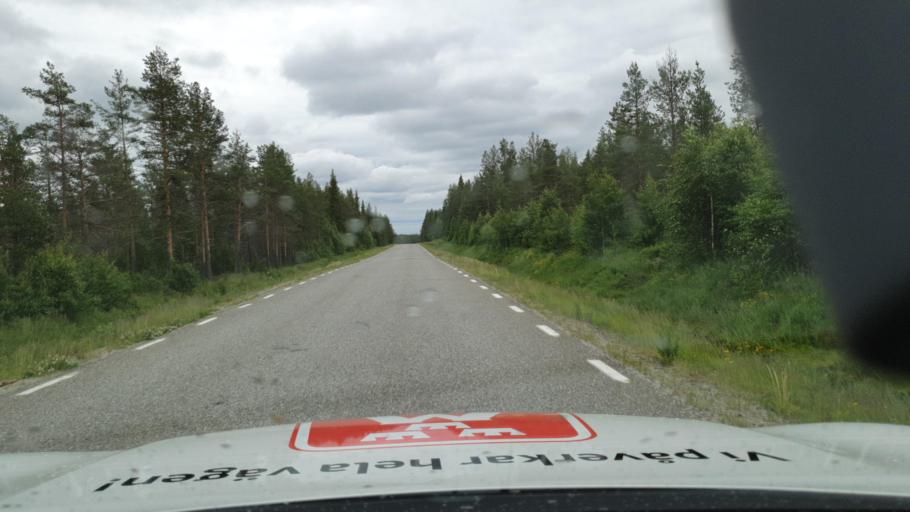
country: SE
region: Vaesterbotten
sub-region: Lycksele Kommun
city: Soderfors
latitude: 64.2645
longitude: 18.2049
